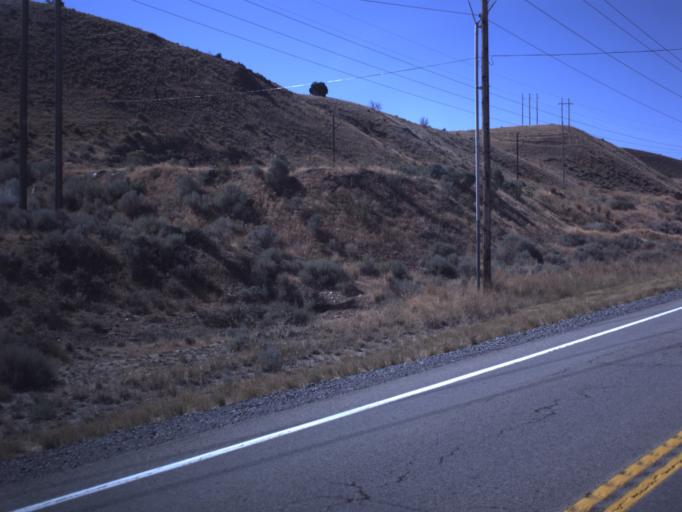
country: US
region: Utah
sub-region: Tooele County
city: Tooele
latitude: 40.4791
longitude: -112.3454
